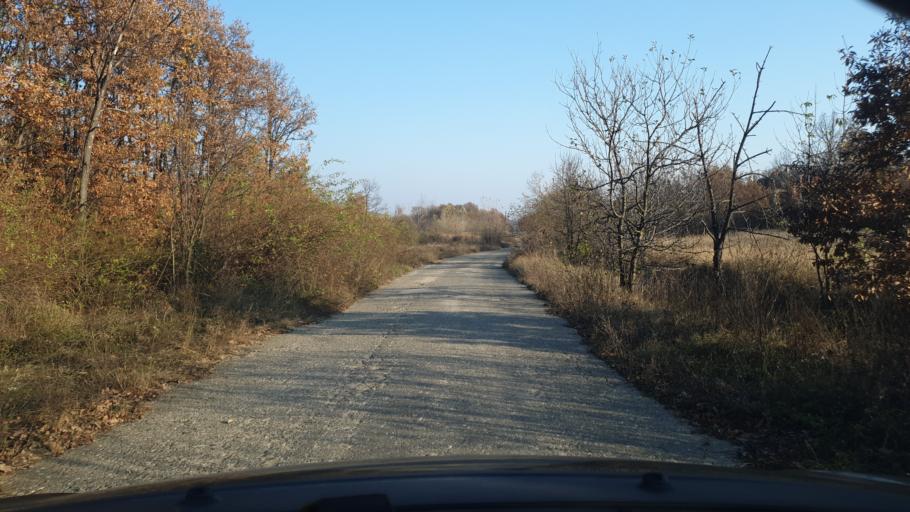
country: RS
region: Central Serbia
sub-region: Borski Okrug
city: Negotin
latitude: 44.1485
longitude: 22.3516
